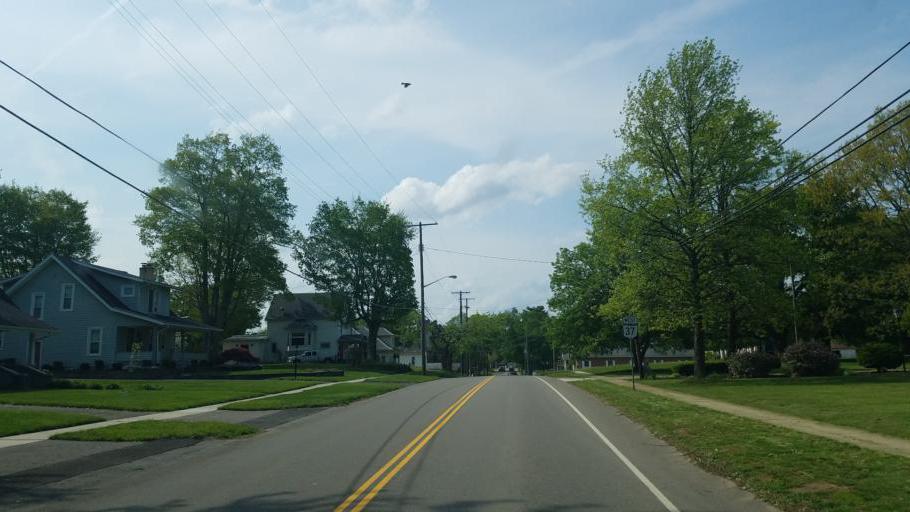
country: US
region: Ohio
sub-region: Licking County
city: Johnstown
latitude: 40.1479
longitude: -82.6790
